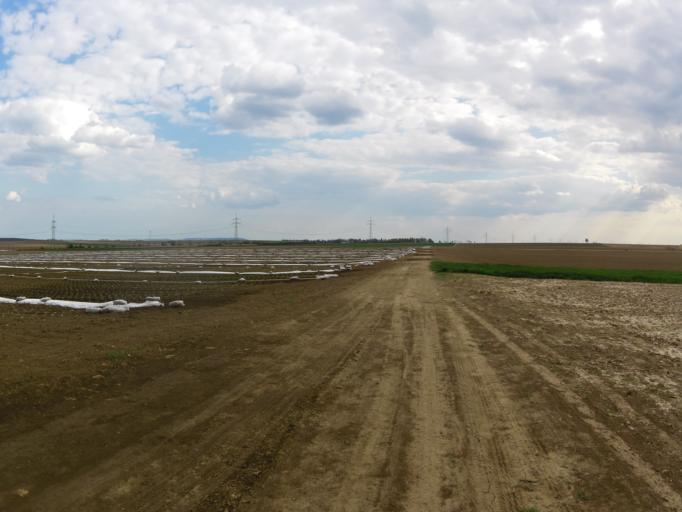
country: DE
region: Bavaria
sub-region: Regierungsbezirk Unterfranken
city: Oberpleichfeld
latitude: 49.8722
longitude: 10.0912
